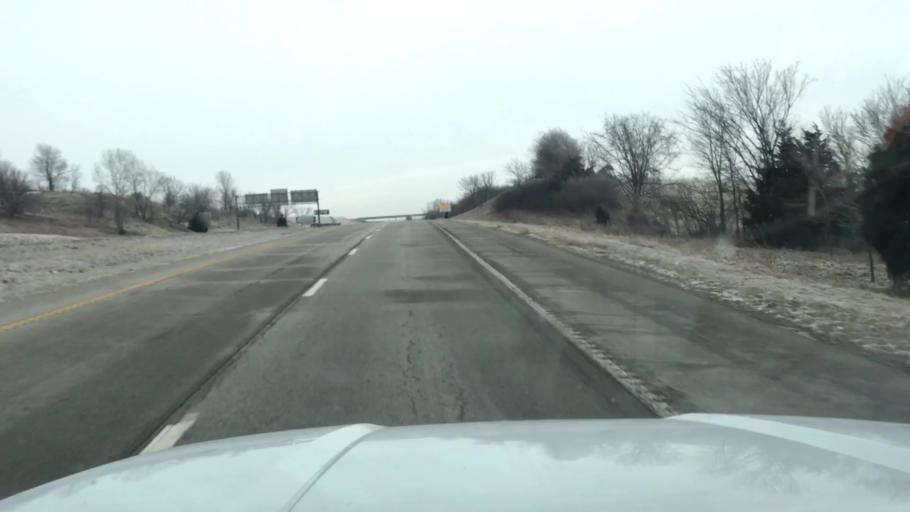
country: US
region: Missouri
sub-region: Andrew County
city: Savannah
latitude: 39.8905
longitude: -94.8570
